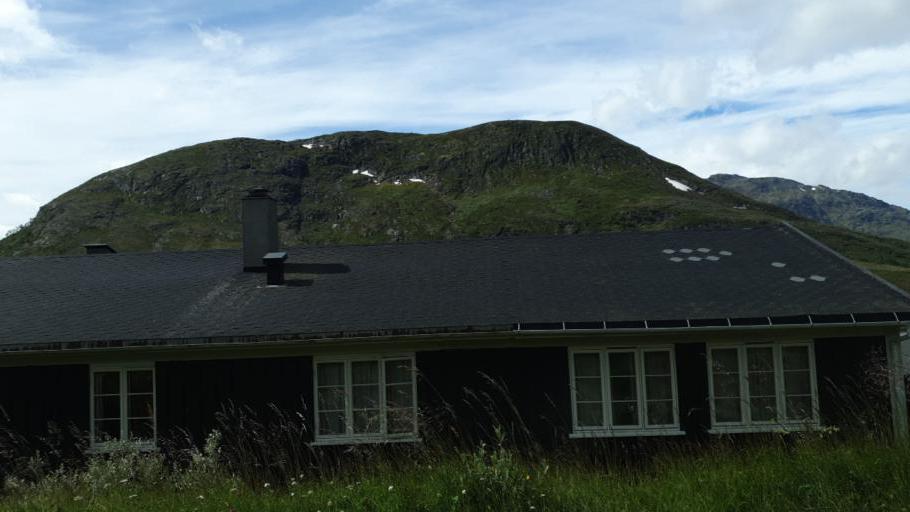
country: NO
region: Oppland
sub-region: Lom
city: Fossbergom
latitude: 61.4941
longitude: 8.8140
